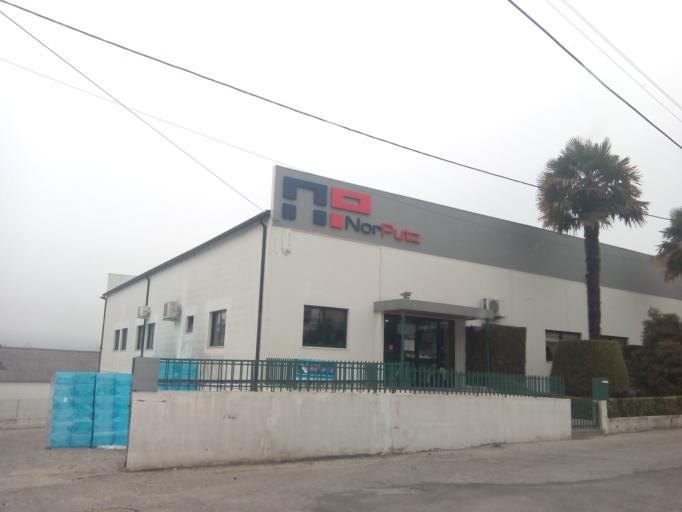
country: PT
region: Porto
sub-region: Paredes
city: Casteloes de Cepeda
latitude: 41.2005
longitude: -8.3398
